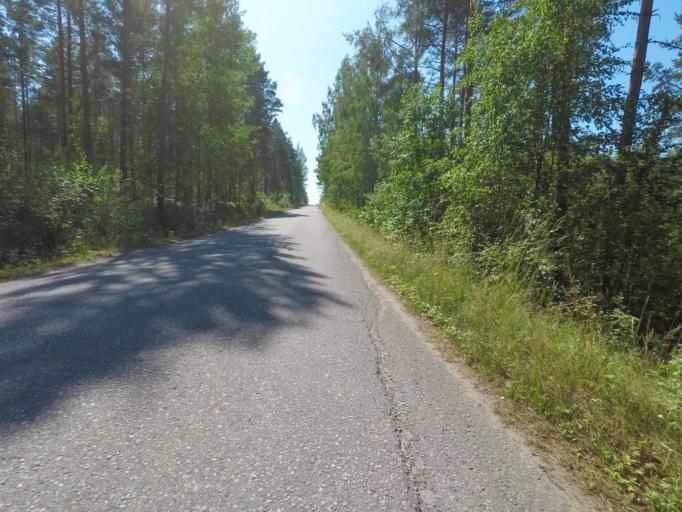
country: FI
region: Southern Savonia
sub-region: Mikkeli
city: Puumala
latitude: 61.4193
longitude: 28.0932
